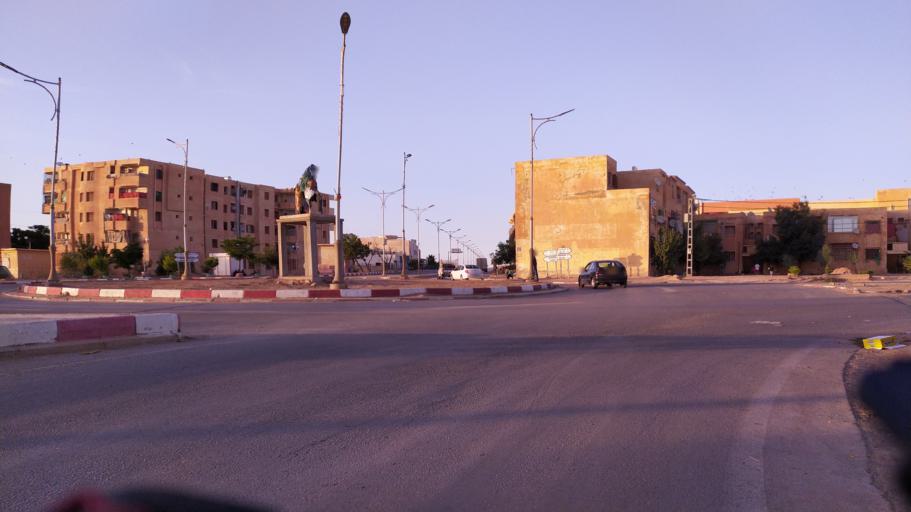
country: DZ
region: Tiaret
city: Frenda
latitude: 34.8968
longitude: 1.2479
